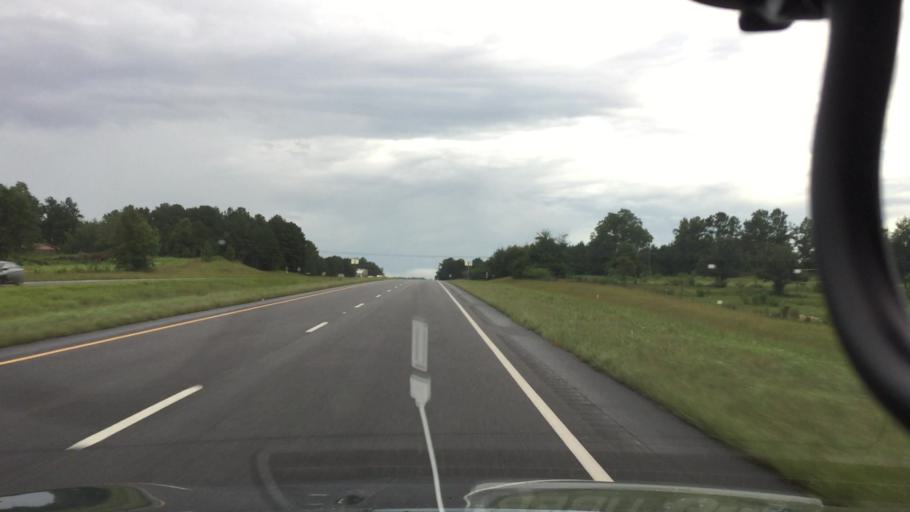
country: US
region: Alabama
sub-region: Pike County
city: Troy
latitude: 31.8857
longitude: -86.0070
